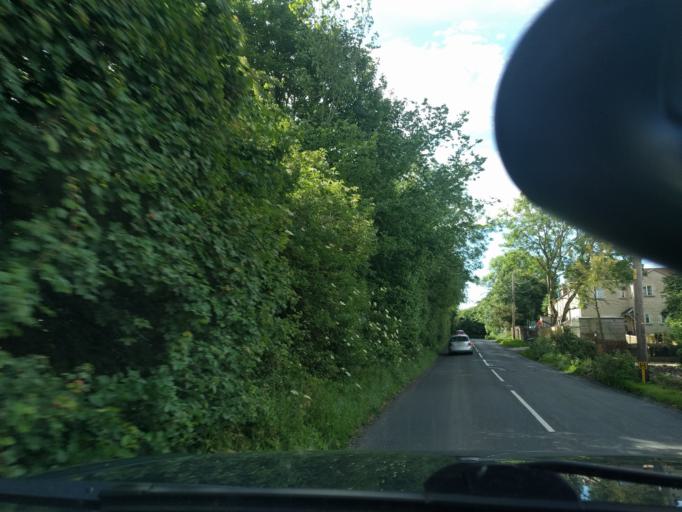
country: GB
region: England
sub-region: Wiltshire
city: Bradford-on-Avon
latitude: 51.3641
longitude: -2.2352
